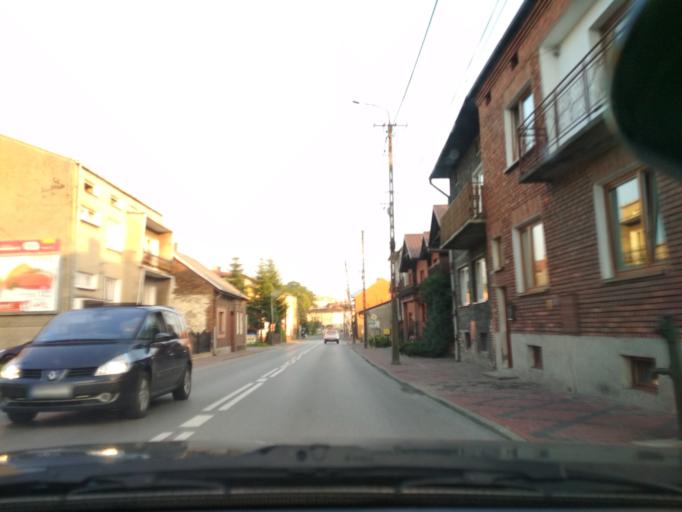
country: PL
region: Lesser Poland Voivodeship
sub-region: Powiat olkuski
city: Wolbrom
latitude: 50.3891
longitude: 19.7573
